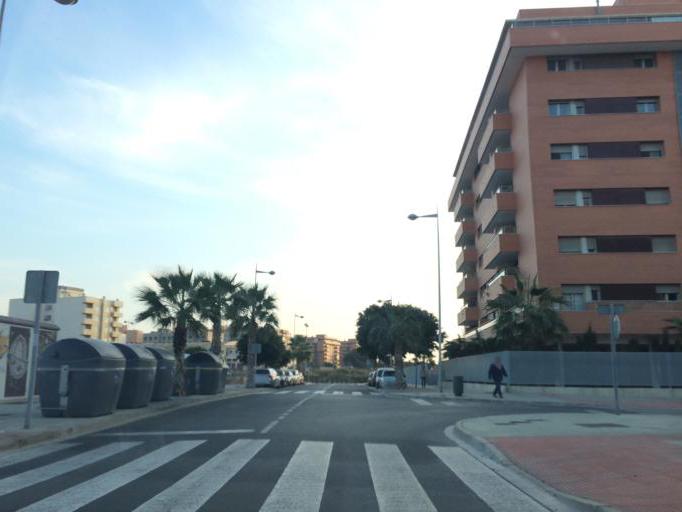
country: ES
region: Andalusia
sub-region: Provincia de Almeria
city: Almeria
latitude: 36.8352
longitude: -2.4396
